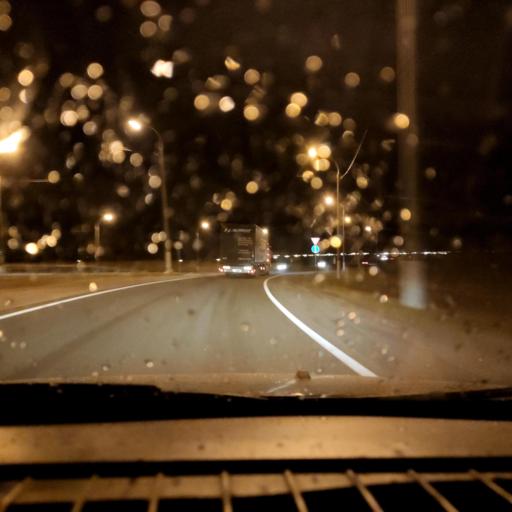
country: RU
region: Samara
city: Zhigulevsk
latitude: 53.5024
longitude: 49.5393
